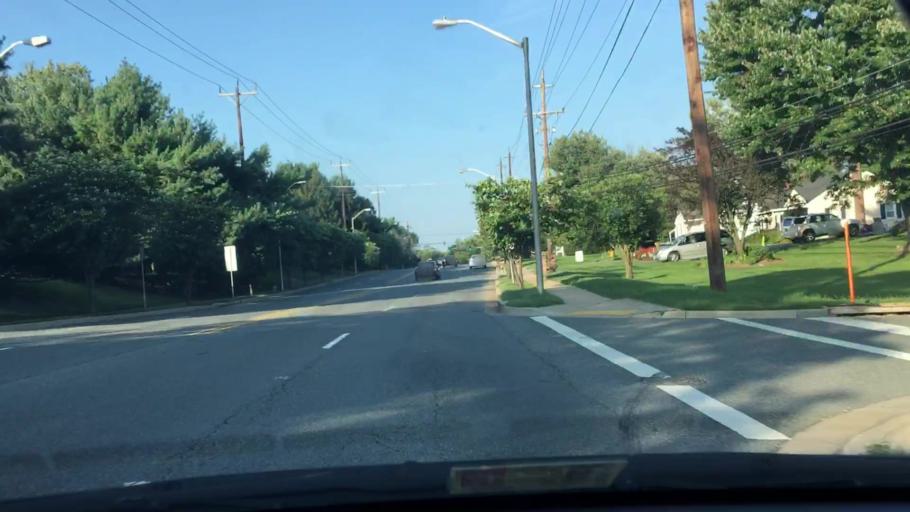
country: US
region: Maryland
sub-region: Montgomery County
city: Derwood
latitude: 39.1230
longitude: -77.1566
